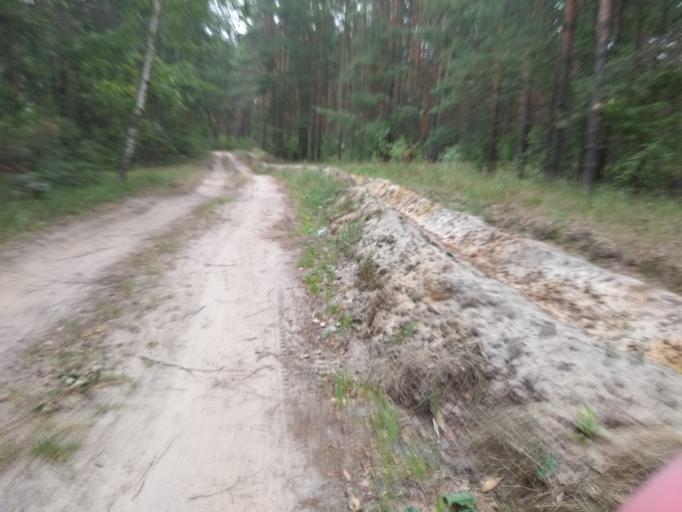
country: RU
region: Moskovskaya
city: Misheronskiy
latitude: 55.6254
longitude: 39.7162
